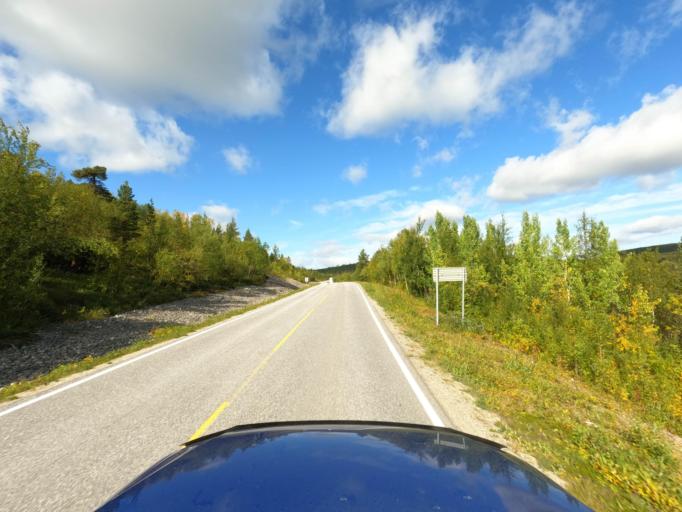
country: NO
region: Finnmark Fylke
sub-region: Karasjok
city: Karasjohka
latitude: 69.4837
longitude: 25.5106
